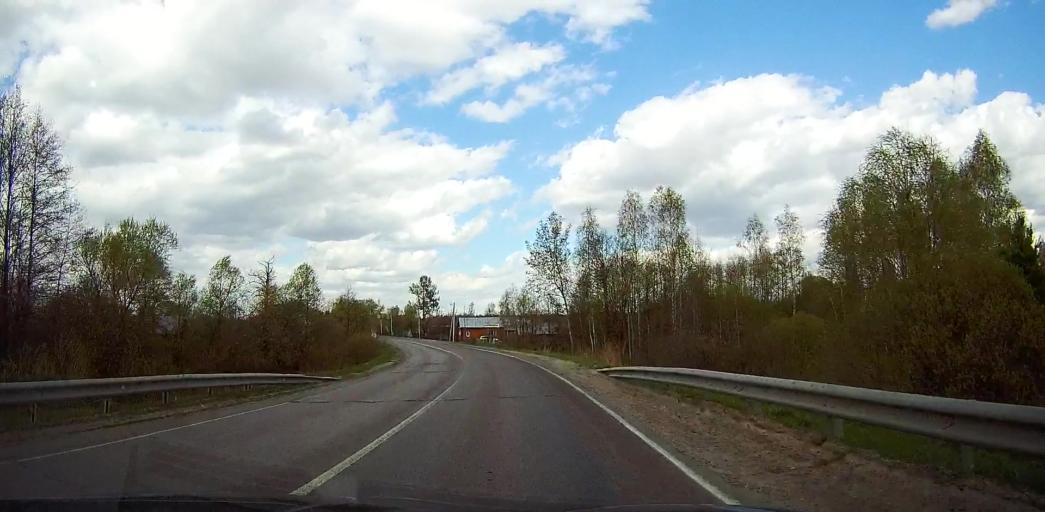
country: RU
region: Moskovskaya
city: Davydovo
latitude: 55.6326
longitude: 38.8684
